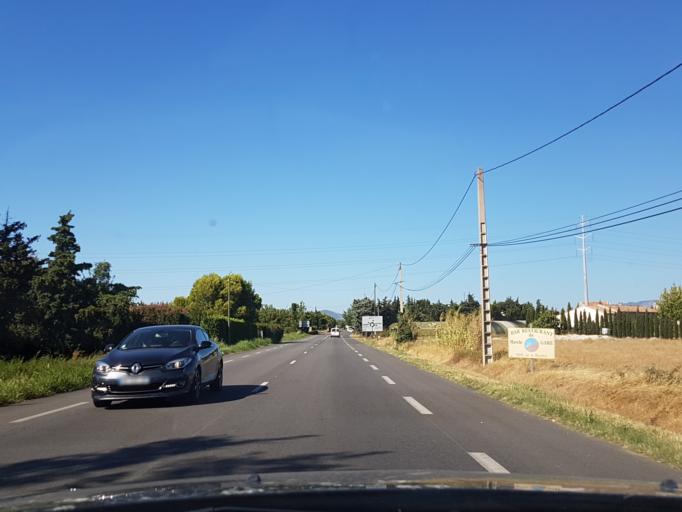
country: FR
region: Provence-Alpes-Cote d'Azur
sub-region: Departement du Vaucluse
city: Carpentras
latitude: 44.0297
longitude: 5.0380
